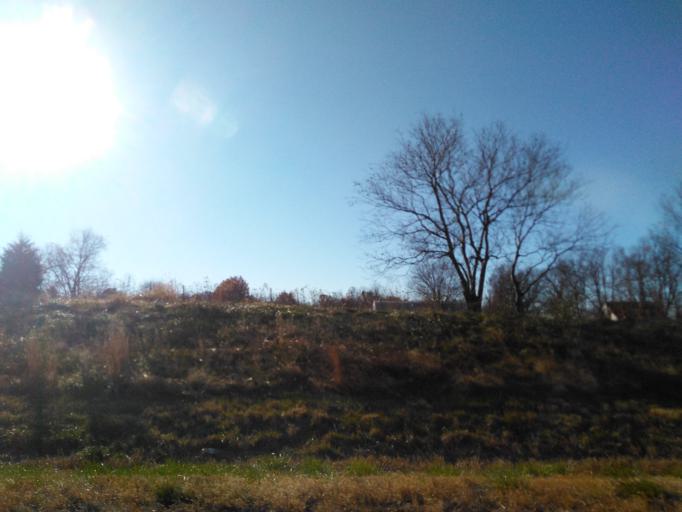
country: US
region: Illinois
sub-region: Madison County
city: Saint Jacob
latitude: 38.7639
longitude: -89.7793
